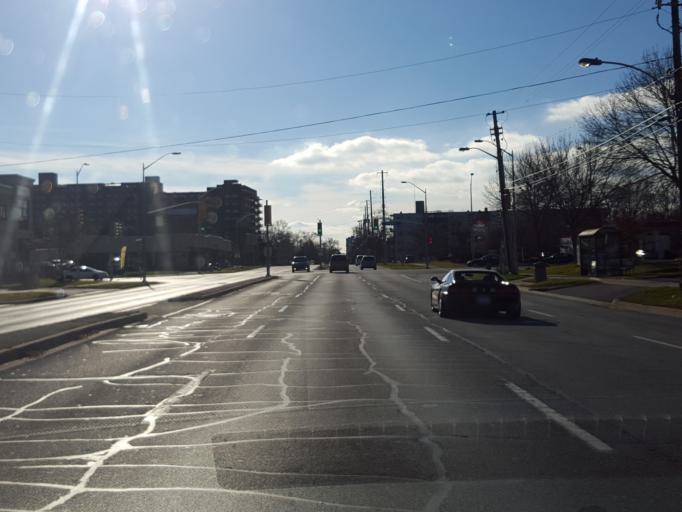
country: CA
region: Ontario
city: Burlington
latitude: 43.3390
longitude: -79.7846
